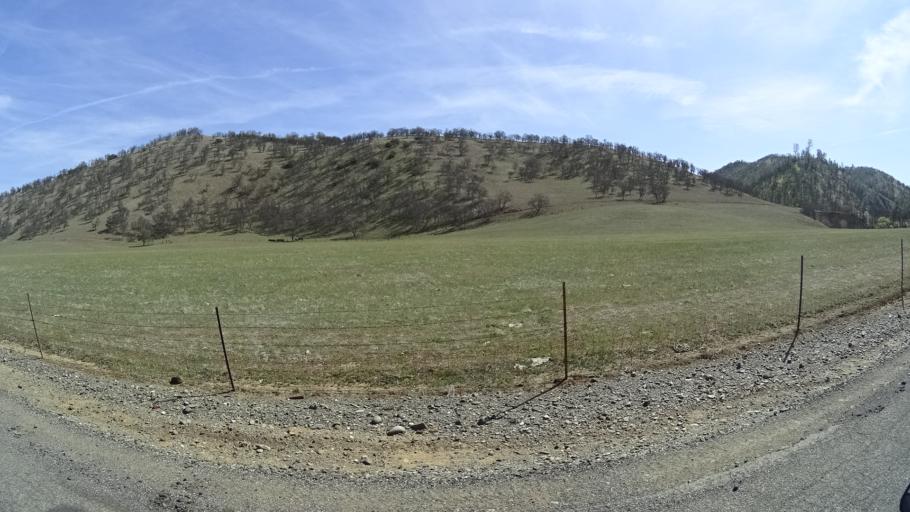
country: US
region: California
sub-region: Glenn County
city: Willows
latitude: 39.4964
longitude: -122.4548
